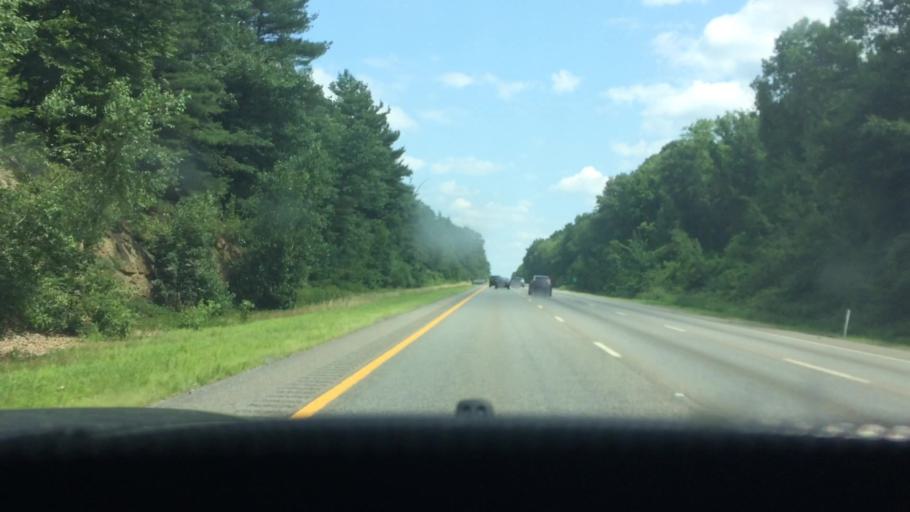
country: US
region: Massachusetts
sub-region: Worcester County
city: Harvard
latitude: 42.4994
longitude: -71.5329
